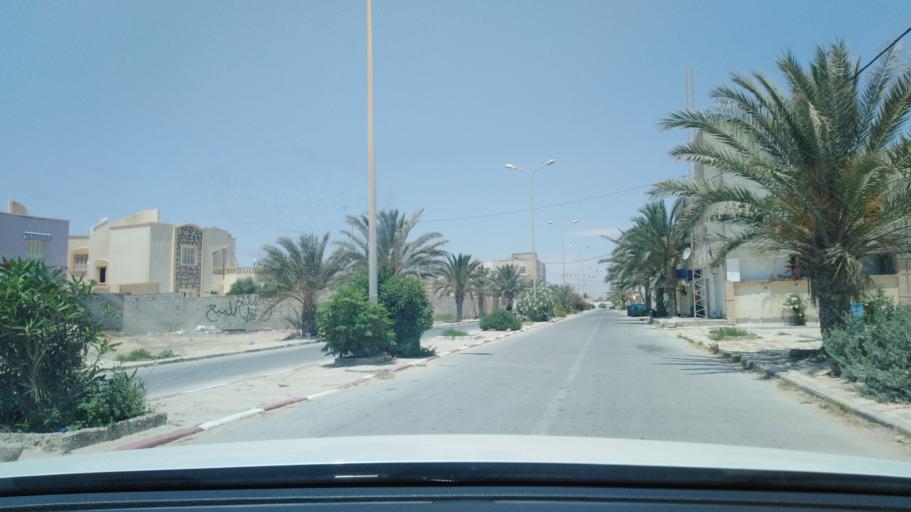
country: TN
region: Qabis
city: Gabes
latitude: 33.9470
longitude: 10.0712
